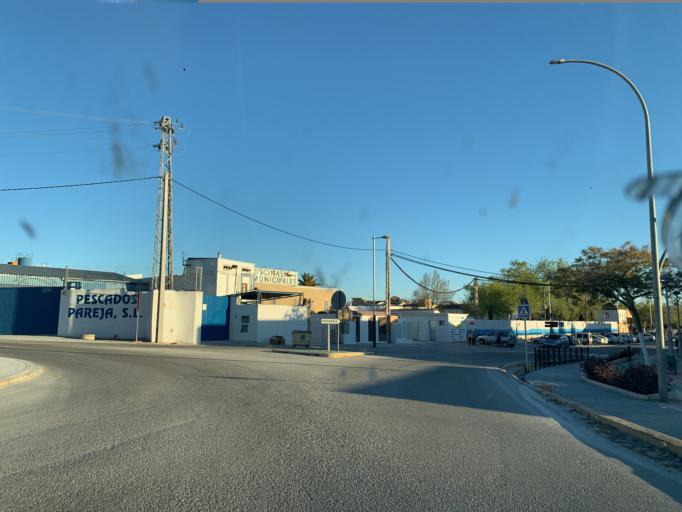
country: ES
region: Andalusia
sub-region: Provincia de Sevilla
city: Pedrera
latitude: 37.2298
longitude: -4.8930
